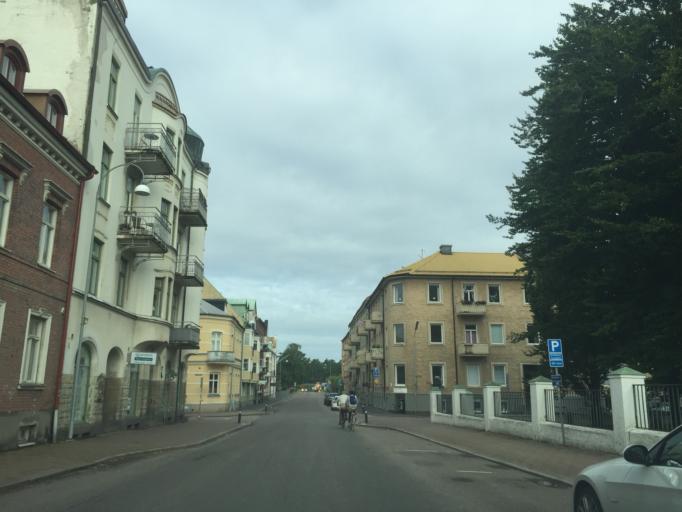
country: SE
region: Skane
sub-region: Angelholms Kommun
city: AEngelholm
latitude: 56.2433
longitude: 12.8593
